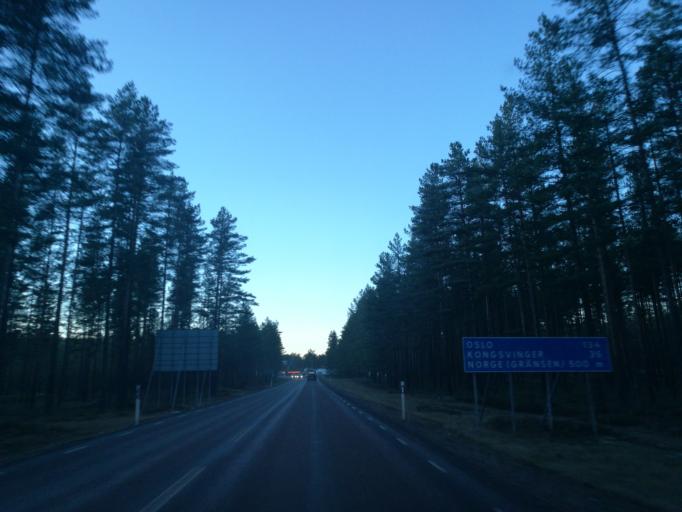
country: SE
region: Vaermland
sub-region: Eda Kommun
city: Charlottenberg
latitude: 59.9284
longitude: 12.2493
